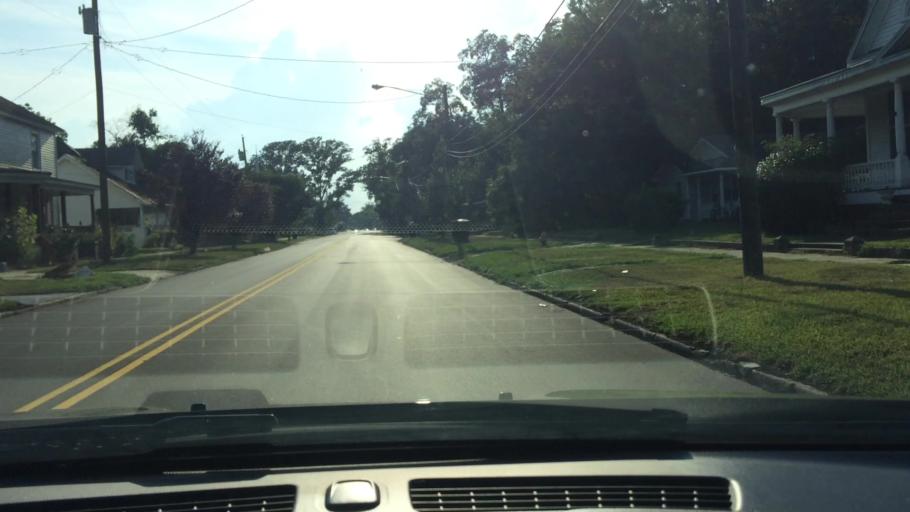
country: US
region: North Carolina
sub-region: Pitt County
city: Ayden
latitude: 35.4709
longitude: -77.4127
